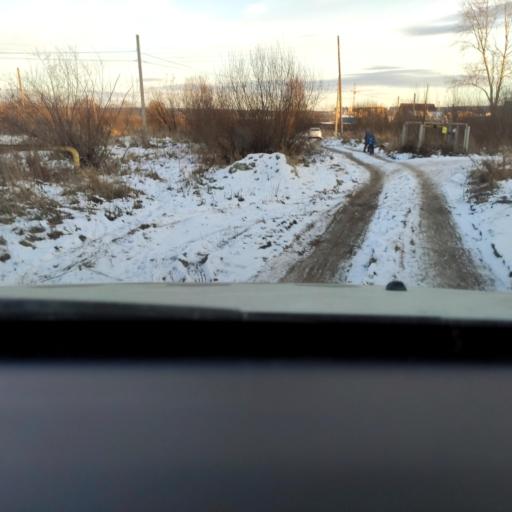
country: RU
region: Perm
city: Ferma
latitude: 57.8998
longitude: 56.3025
